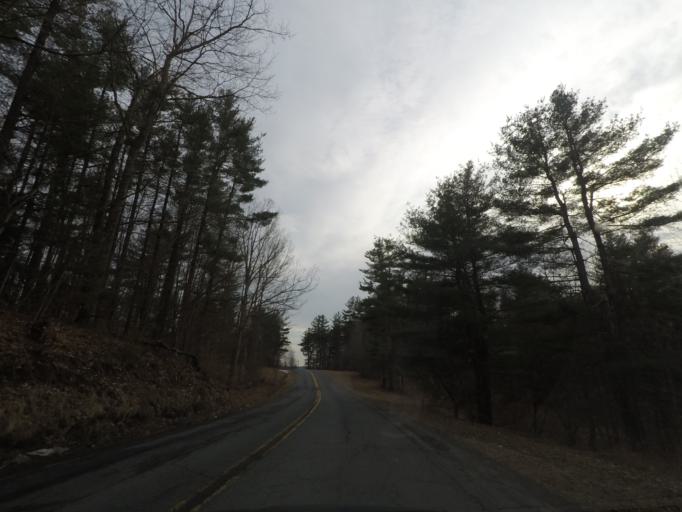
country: US
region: New York
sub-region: Rensselaer County
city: Hoosick Falls
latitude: 42.8552
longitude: -73.4541
